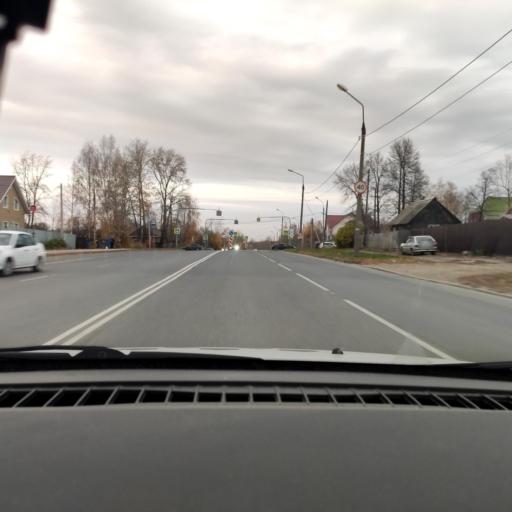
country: RU
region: Perm
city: Polazna
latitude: 58.1221
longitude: 56.4038
